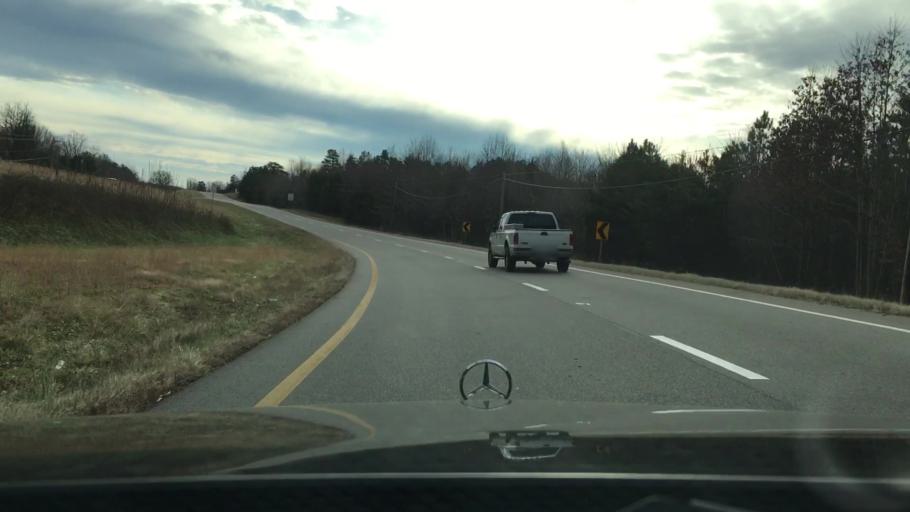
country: US
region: Virginia
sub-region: Pittsylvania County
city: Chatham
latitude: 36.8836
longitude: -79.4081
